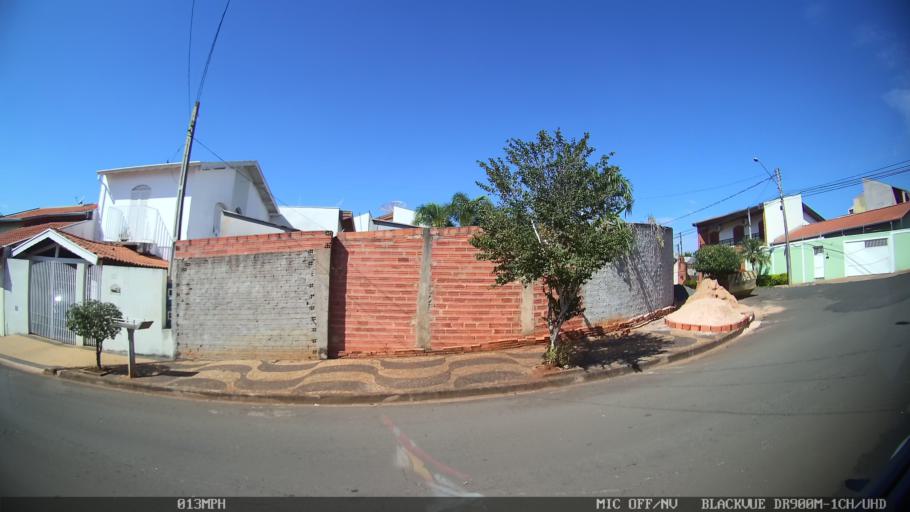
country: BR
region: Sao Paulo
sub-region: Santa Barbara D'Oeste
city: Santa Barbara d'Oeste
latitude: -22.7384
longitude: -47.4215
